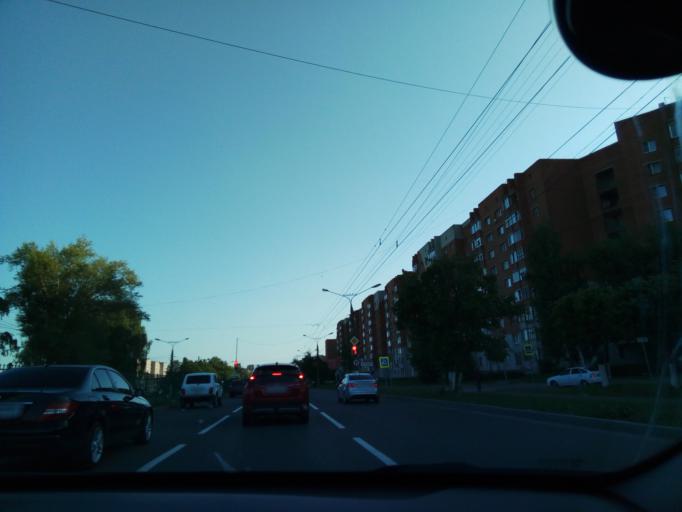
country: RU
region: Chuvashia
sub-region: Cheboksarskiy Rayon
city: Cheboksary
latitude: 56.1156
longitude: 47.2733
